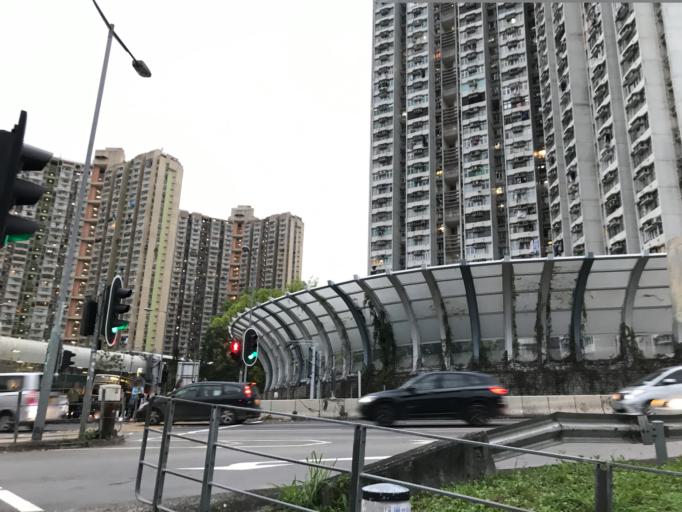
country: HK
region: Tai Po
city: Tai Po
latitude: 22.4521
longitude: 114.1585
